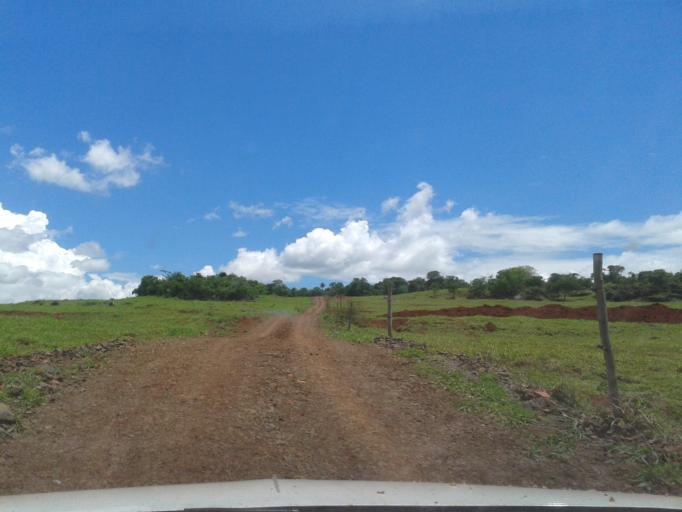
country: BR
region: Minas Gerais
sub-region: Centralina
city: Centralina
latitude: -18.6421
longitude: -49.1921
